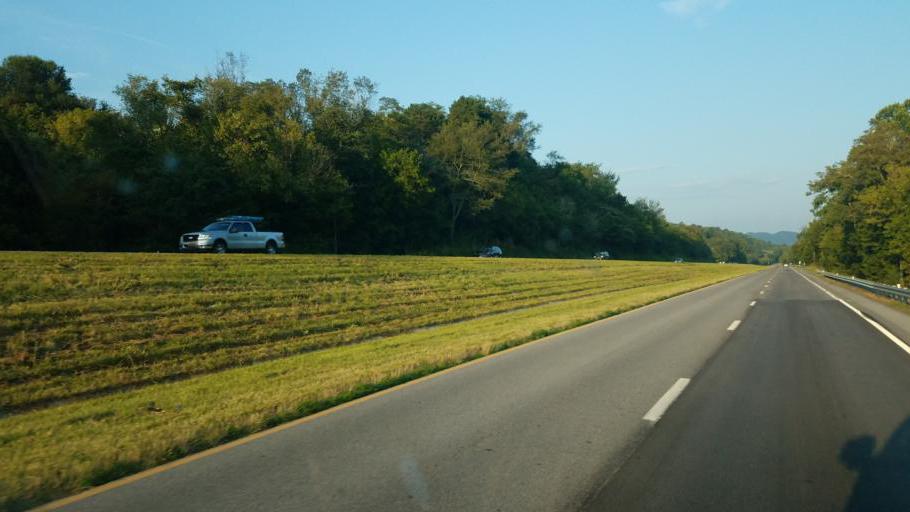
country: US
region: Virginia
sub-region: Scott County
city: Gate City
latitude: 36.6385
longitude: -82.6676
